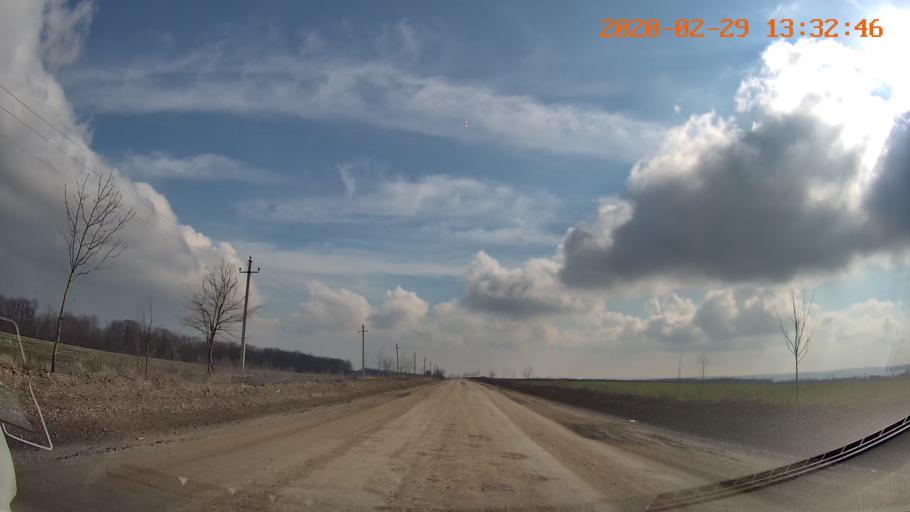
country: MD
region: Telenesti
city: Camenca
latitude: 47.8773
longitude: 28.6119
